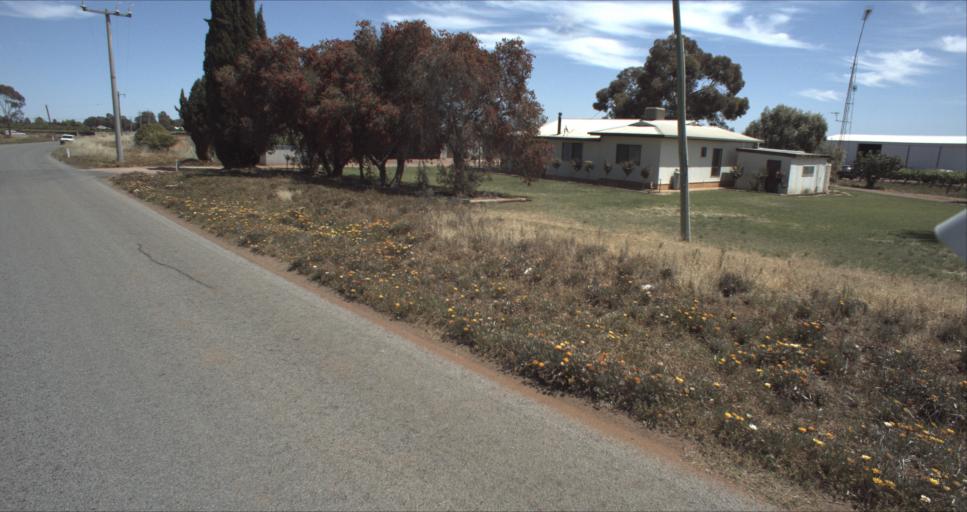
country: AU
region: New South Wales
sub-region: Leeton
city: Leeton
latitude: -34.5696
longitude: 146.4415
